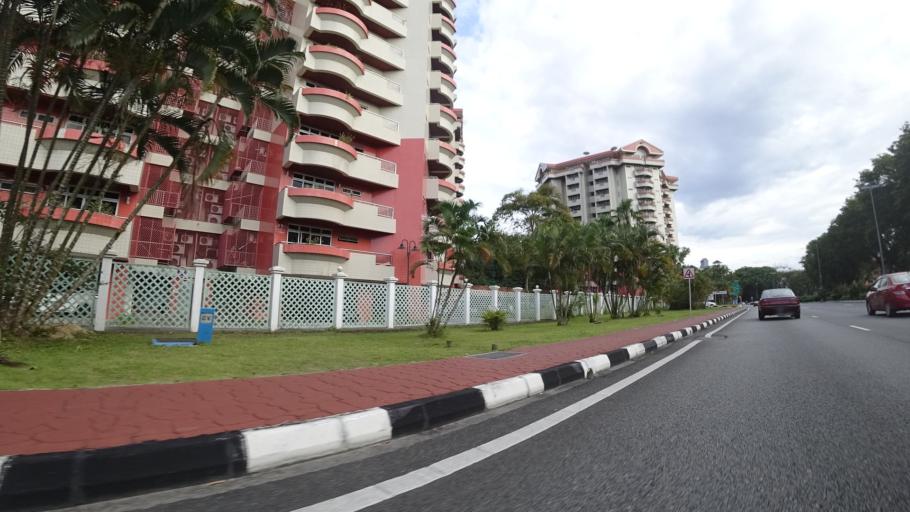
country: BN
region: Brunei and Muara
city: Bandar Seri Begawan
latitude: 4.8994
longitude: 114.9396
